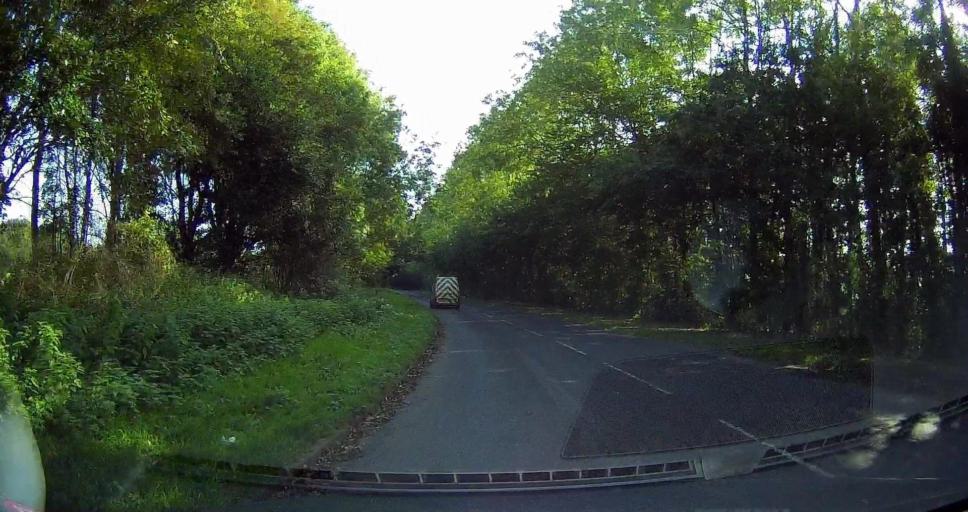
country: GB
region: England
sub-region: Kent
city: Longfield
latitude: 51.3609
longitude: 0.2993
